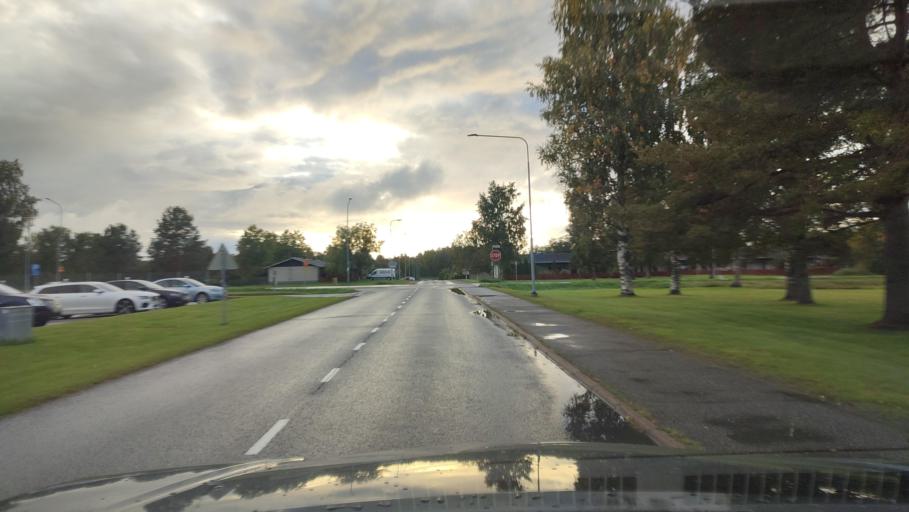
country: FI
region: Ostrobothnia
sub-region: Sydosterbotten
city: Kristinestad
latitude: 62.2800
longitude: 21.3713
